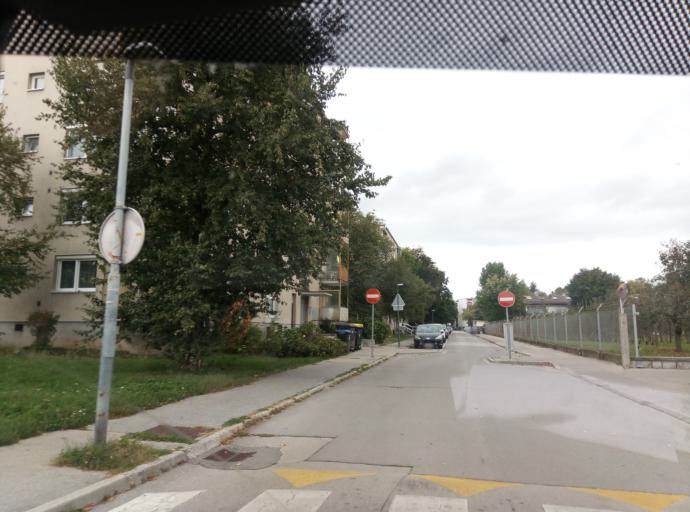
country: SI
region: Ljubljana
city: Ljubljana
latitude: 46.0607
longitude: 14.5179
